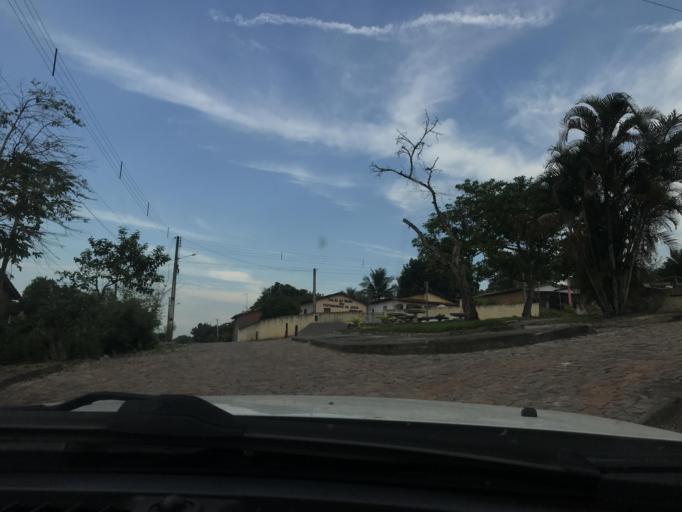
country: BR
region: Bahia
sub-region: Entre Rios
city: Entre Rios
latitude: -12.0119
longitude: -38.2173
